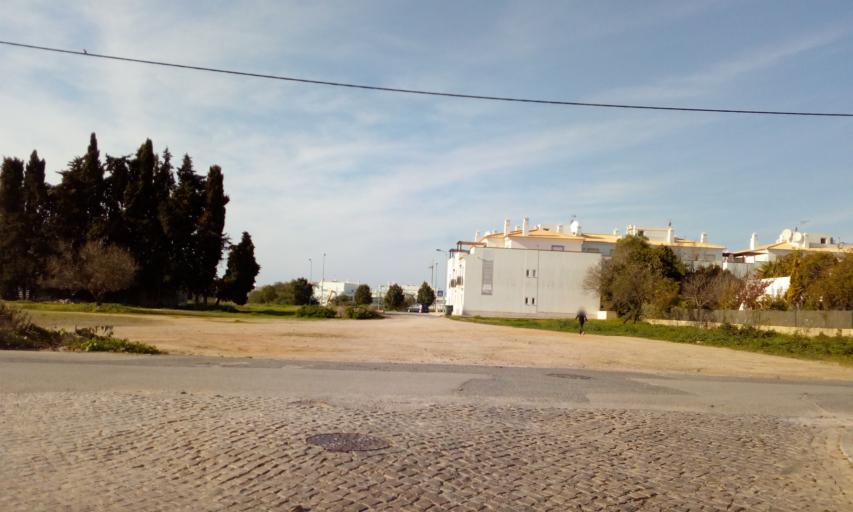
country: PT
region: Faro
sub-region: Tavira
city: Tavira
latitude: 37.1377
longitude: -7.5965
